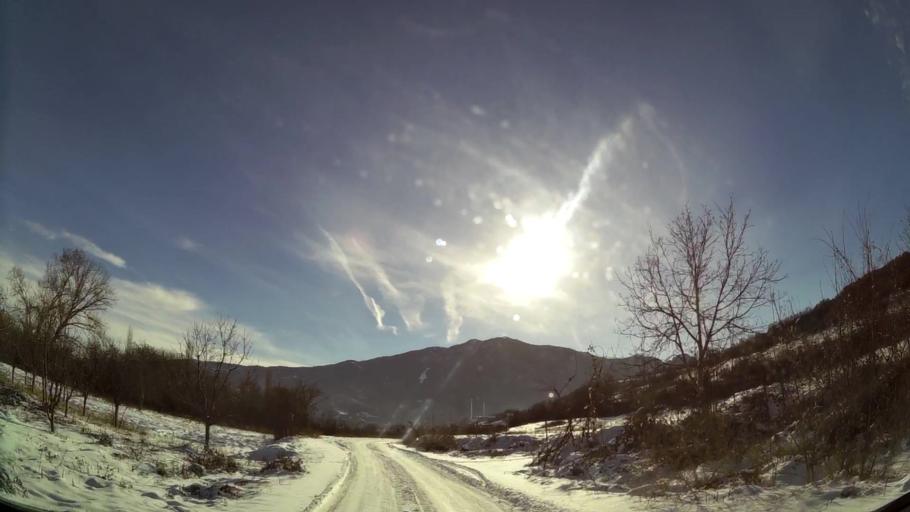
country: MK
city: Ljubin
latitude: 41.9847
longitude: 21.2979
